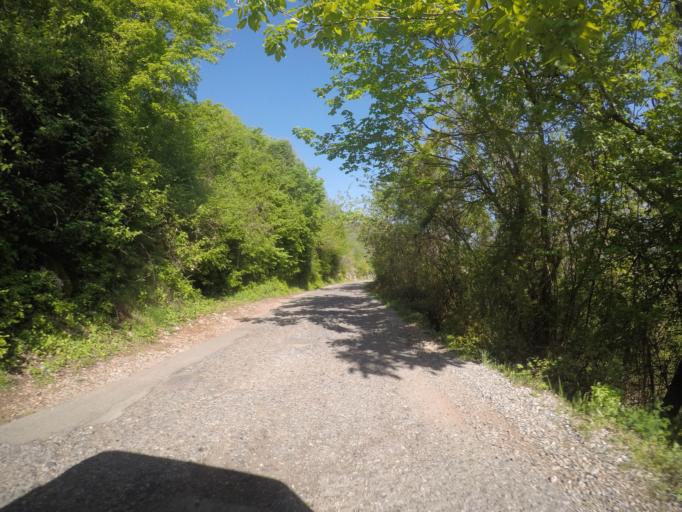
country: ME
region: Danilovgrad
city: Danilovgrad
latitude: 42.5298
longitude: 19.0919
